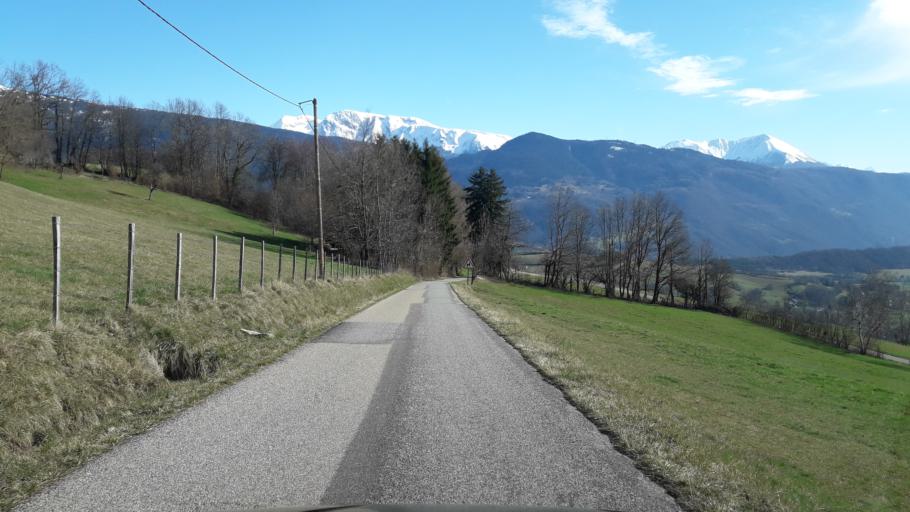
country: FR
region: Rhone-Alpes
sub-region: Departement de l'Isere
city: Herbeys
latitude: 45.1536
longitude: 5.7944
